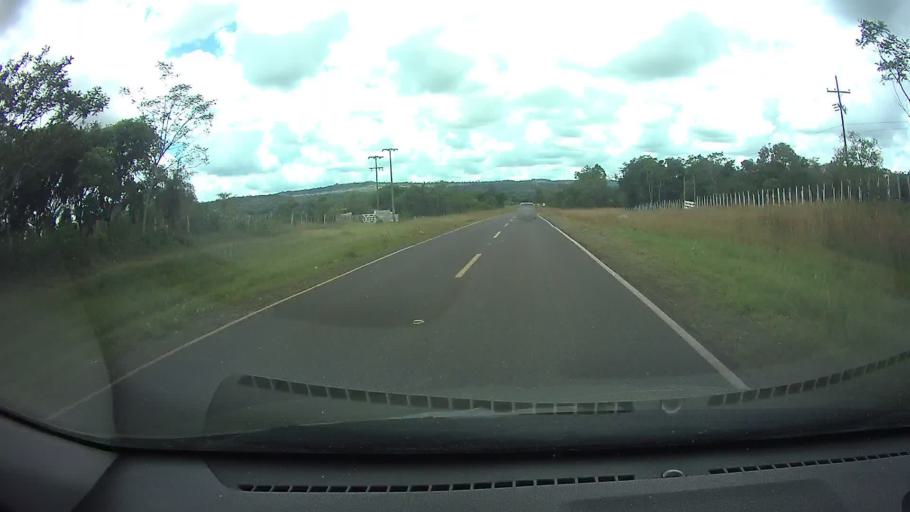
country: PY
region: Paraguari
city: Ybycui
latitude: -25.9045
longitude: -56.9776
